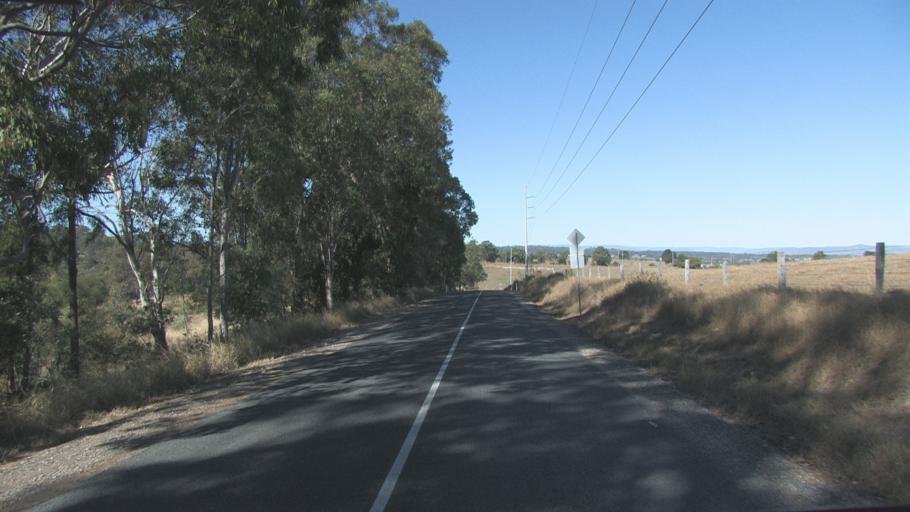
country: AU
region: Queensland
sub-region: Logan
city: Cedar Vale
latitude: -27.8964
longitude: 153.0145
